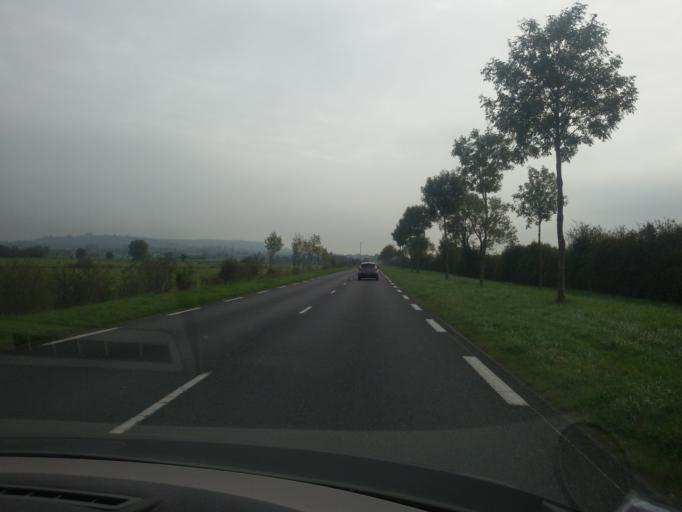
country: FR
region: Lower Normandy
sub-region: Departement du Calvados
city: Dives-sur-Mer
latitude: 49.2394
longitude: -0.0969
